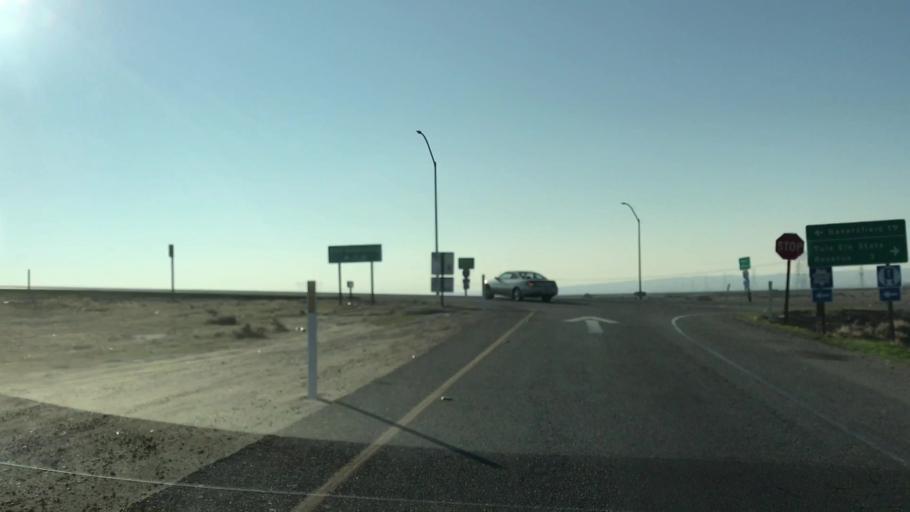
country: US
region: California
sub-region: Kern County
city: Buttonwillow
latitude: 35.3552
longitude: -119.3380
